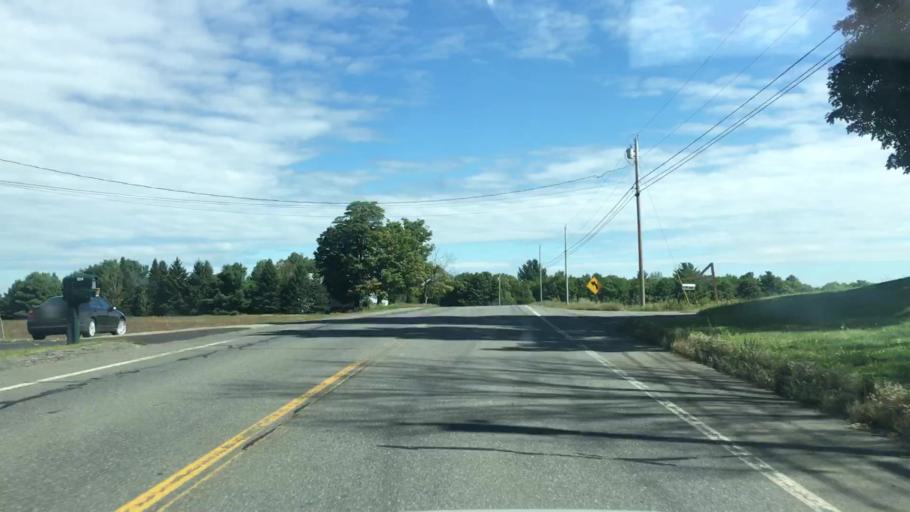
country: US
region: Maine
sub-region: Penobscot County
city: Dexter
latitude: 45.0744
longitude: -69.2339
